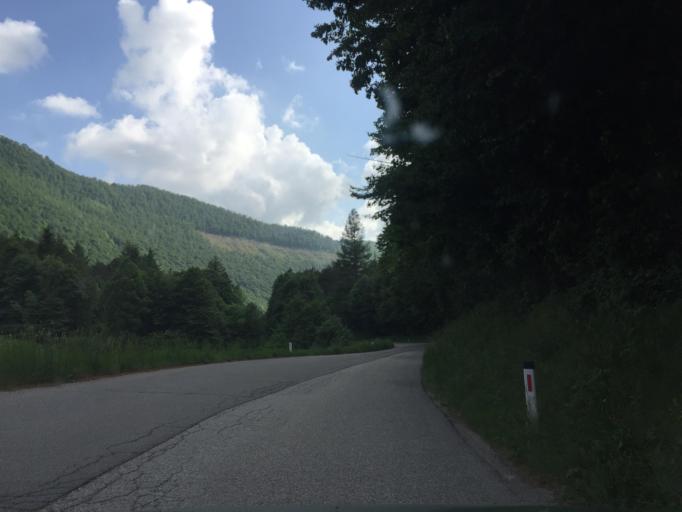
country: SI
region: Nova Gorica
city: Sempas
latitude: 46.0288
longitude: 13.7801
